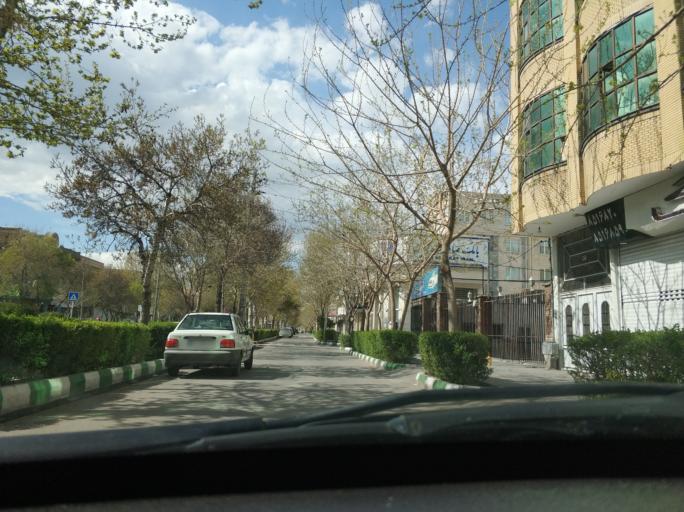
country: IR
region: Razavi Khorasan
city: Mashhad
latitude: 36.2711
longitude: 59.5959
